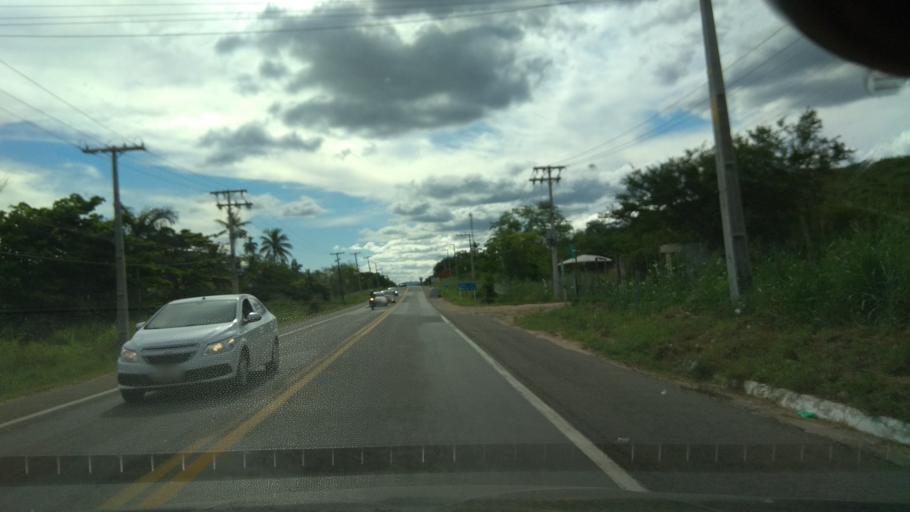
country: BR
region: Bahia
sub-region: Jequie
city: Jequie
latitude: -13.8791
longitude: -40.0357
